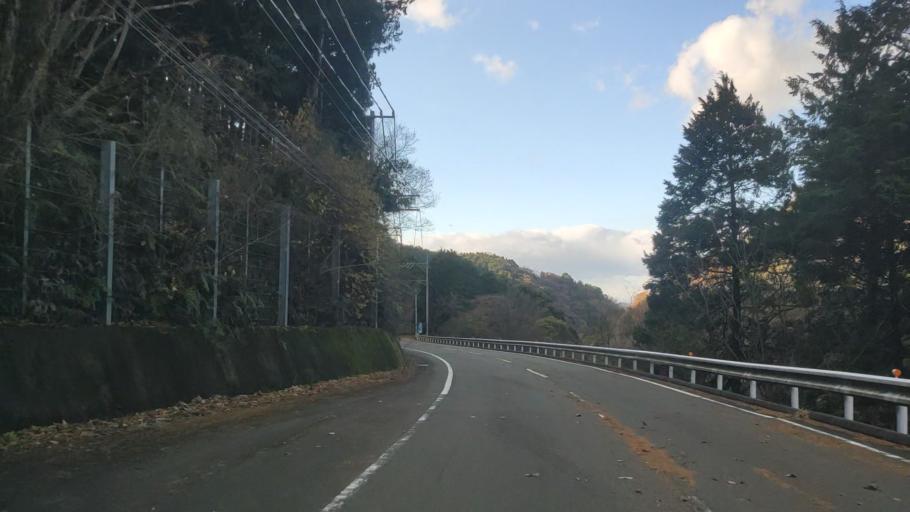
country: JP
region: Ehime
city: Saijo
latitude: 33.8781
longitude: 133.1365
